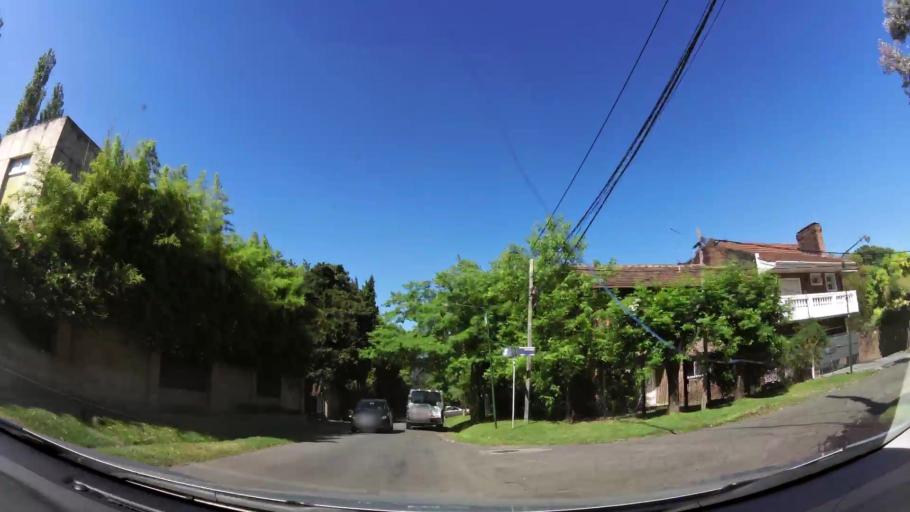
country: AR
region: Buenos Aires
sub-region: Partido de Tigre
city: Tigre
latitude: -34.4875
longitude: -58.5687
